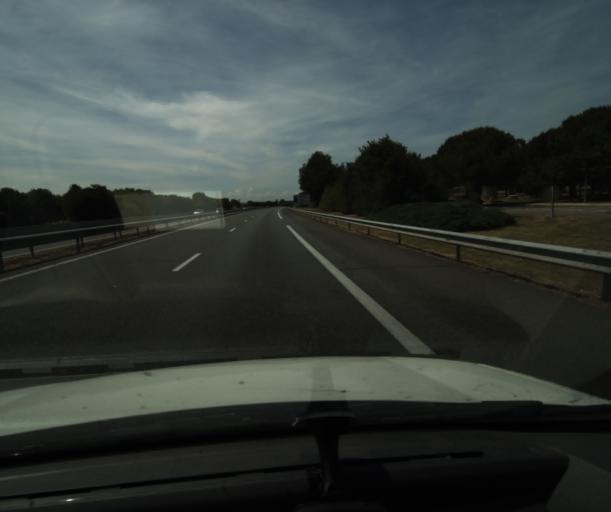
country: FR
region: Languedoc-Roussillon
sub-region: Departement de l'Aude
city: Bram
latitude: 43.2285
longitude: 2.1165
